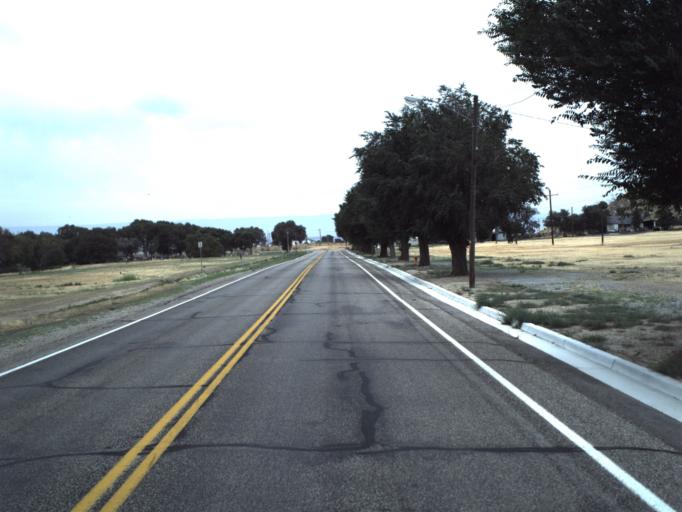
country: US
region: Utah
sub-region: Carbon County
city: East Carbon City
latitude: 39.5496
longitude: -110.3940
